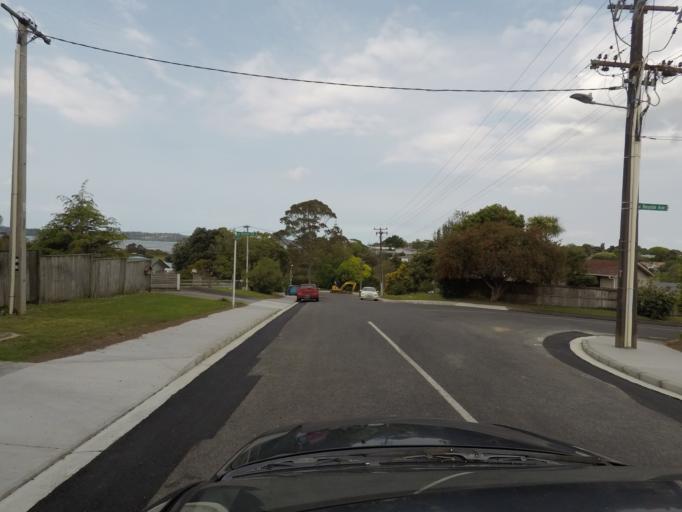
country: NZ
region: Auckland
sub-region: Auckland
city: Rosebank
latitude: -36.8287
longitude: 174.6518
